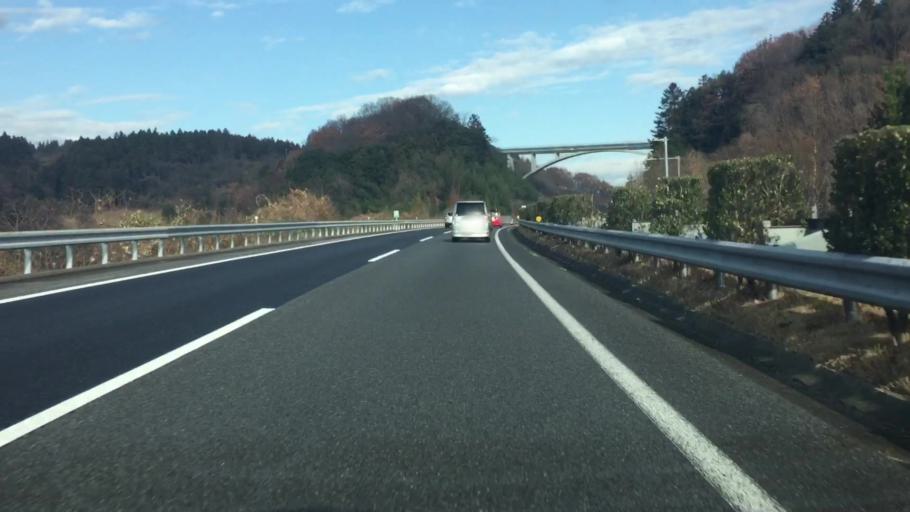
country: JP
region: Gunma
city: Tomioka
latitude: 36.2628
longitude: 138.8142
